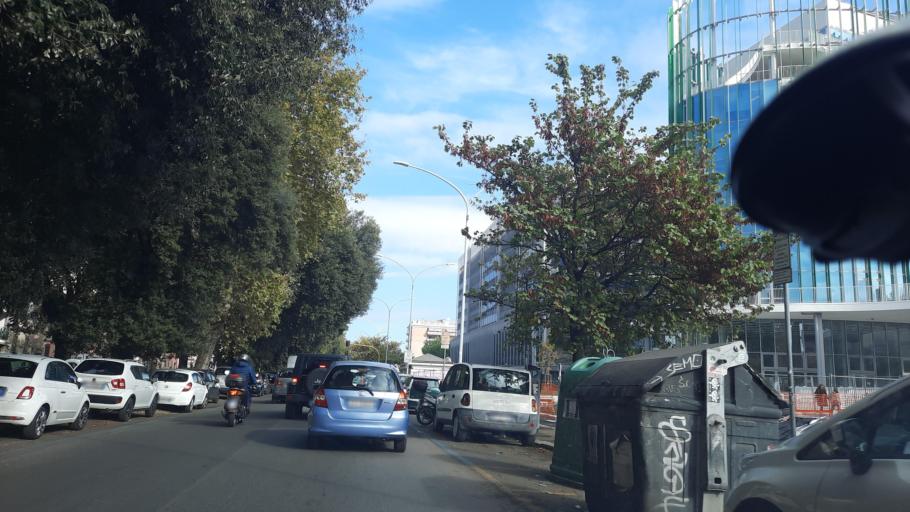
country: IT
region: Latium
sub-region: Citta metropolitana di Roma Capitale
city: Rome
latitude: 41.8644
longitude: 12.4791
